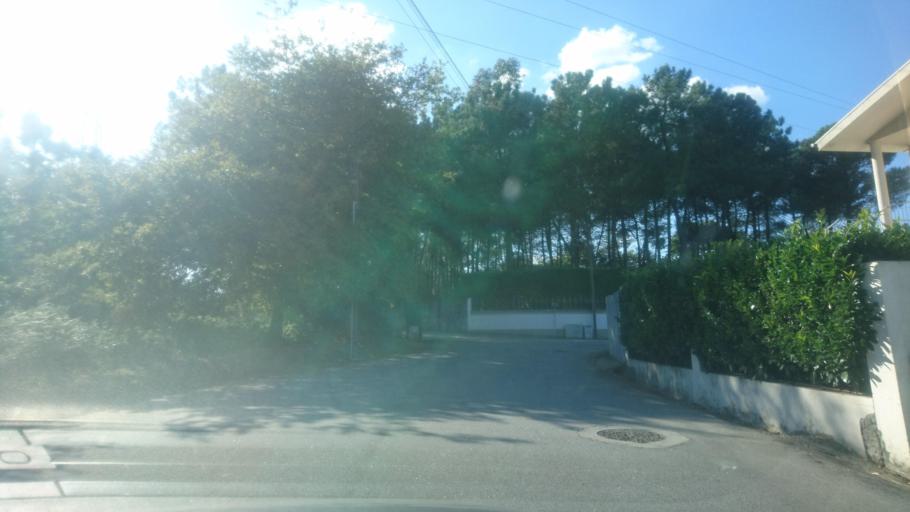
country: PT
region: Porto
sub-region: Paredes
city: Madalena
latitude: 41.2215
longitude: -8.3394
